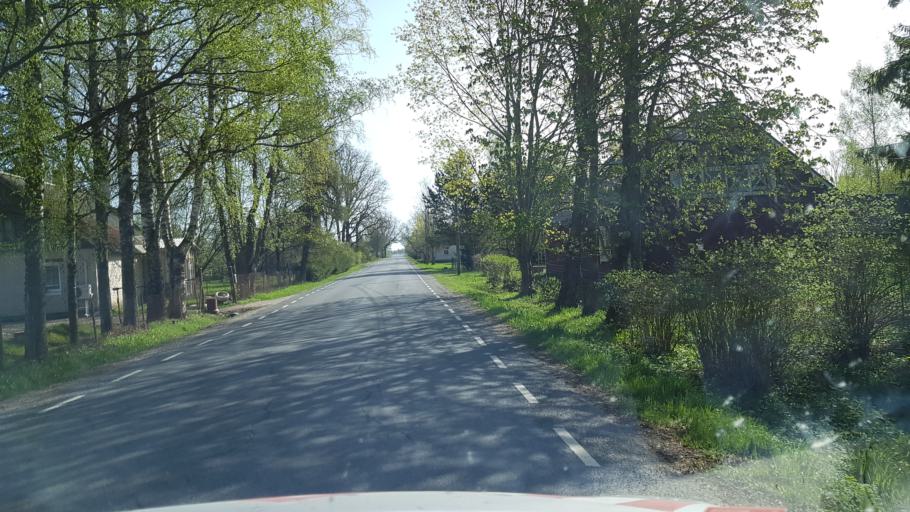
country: EE
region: Viljandimaa
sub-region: Abja vald
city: Abja-Paluoja
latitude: 58.1644
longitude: 25.4421
